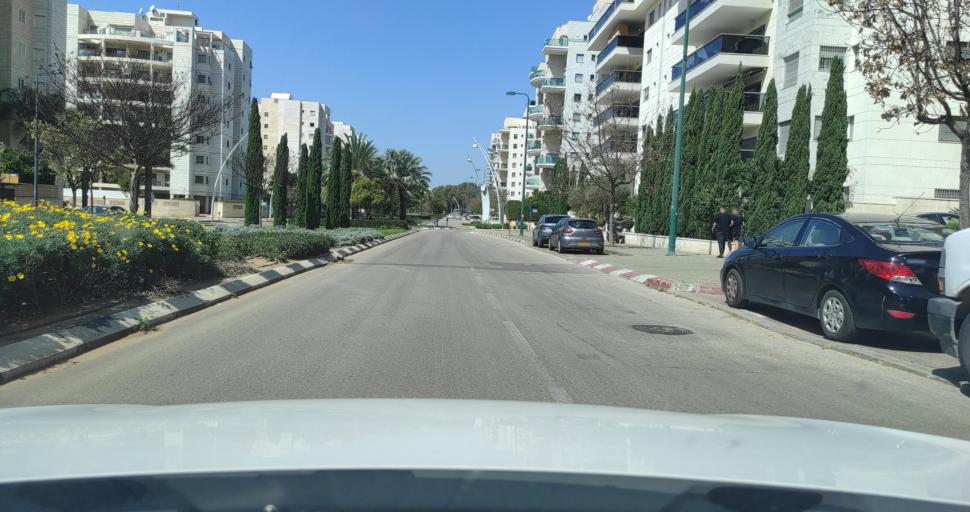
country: IL
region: Central District
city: Nordiyya
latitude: 32.2994
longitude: 34.8736
